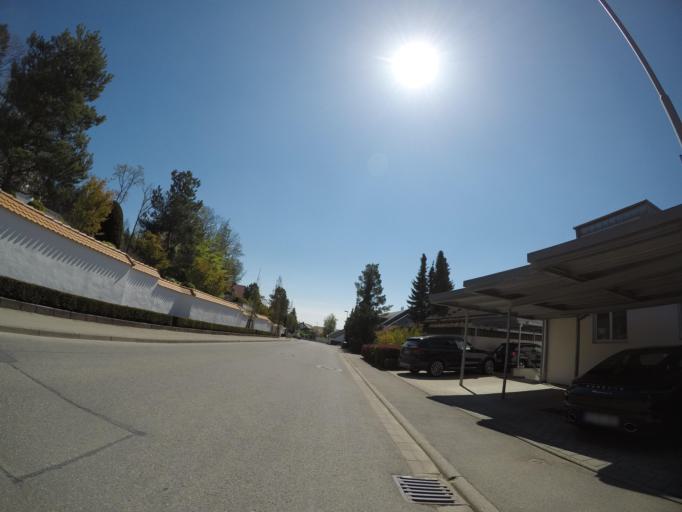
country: DE
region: Baden-Wuerttemberg
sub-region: Tuebingen Region
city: Markdorf
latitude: 47.7350
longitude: 9.3860
